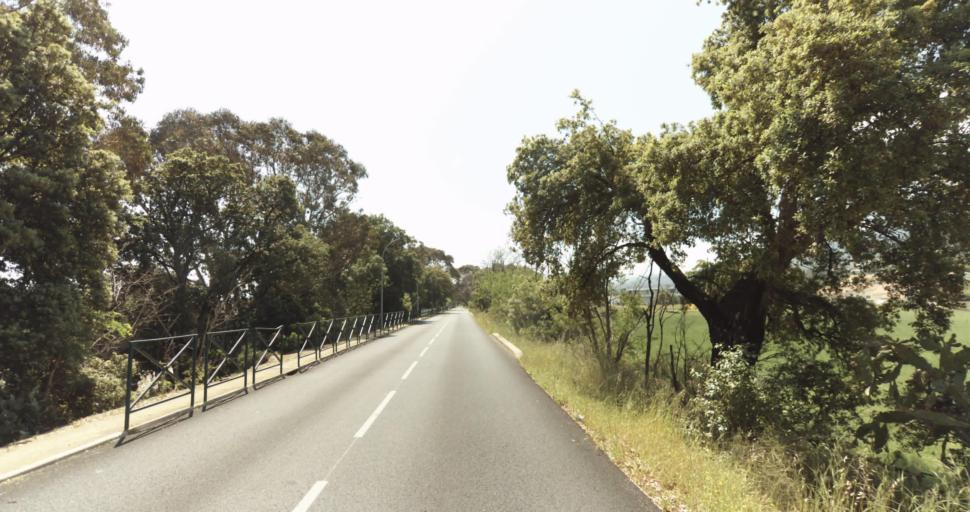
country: FR
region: Corsica
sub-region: Departement de la Haute-Corse
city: Biguglia
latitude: 42.6023
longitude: 9.4345
